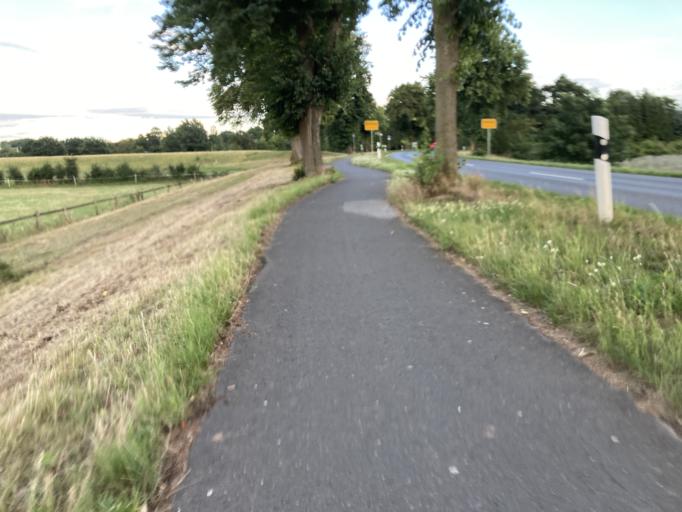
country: DE
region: Lower Saxony
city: Verden
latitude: 52.9002
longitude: 9.2302
